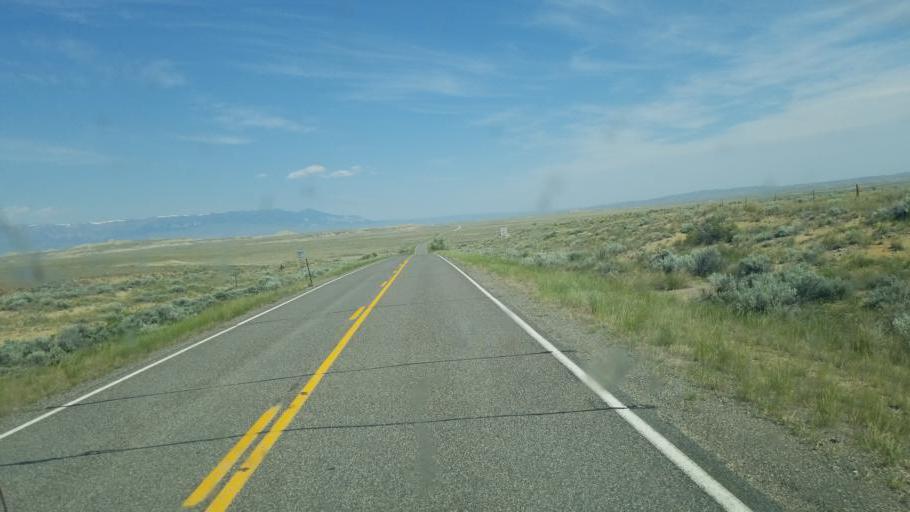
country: US
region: Wyoming
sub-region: Park County
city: Powell
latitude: 44.8027
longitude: -108.9624
